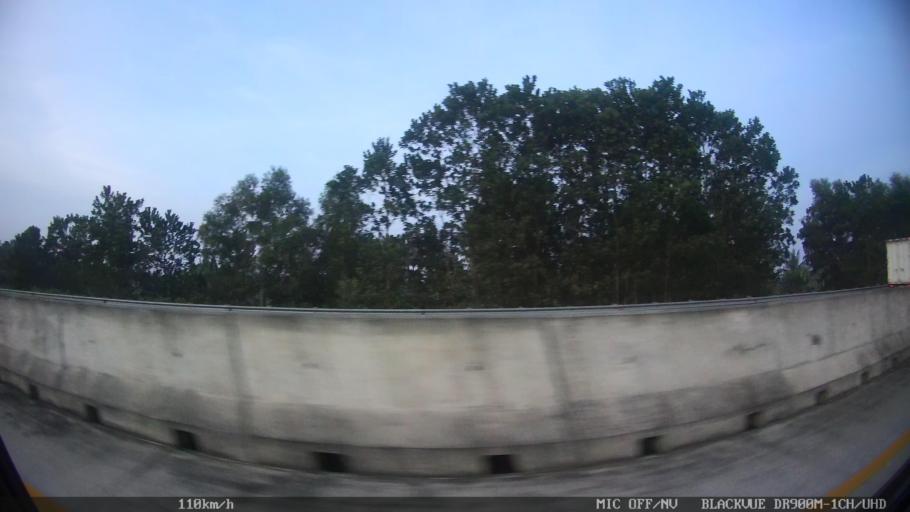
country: ID
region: Lampung
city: Pasuruan
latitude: -5.7355
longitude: 105.6881
